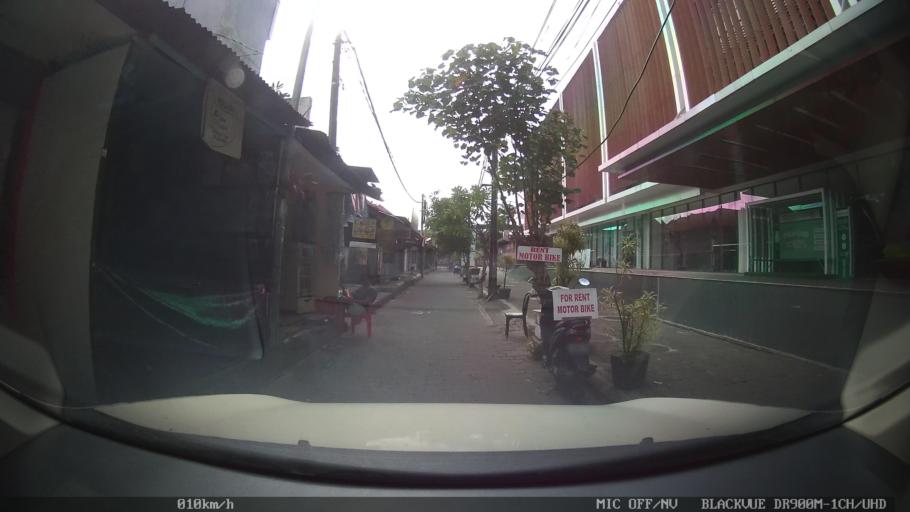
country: ID
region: Bali
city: Jabajero
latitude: -8.7347
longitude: 115.1664
